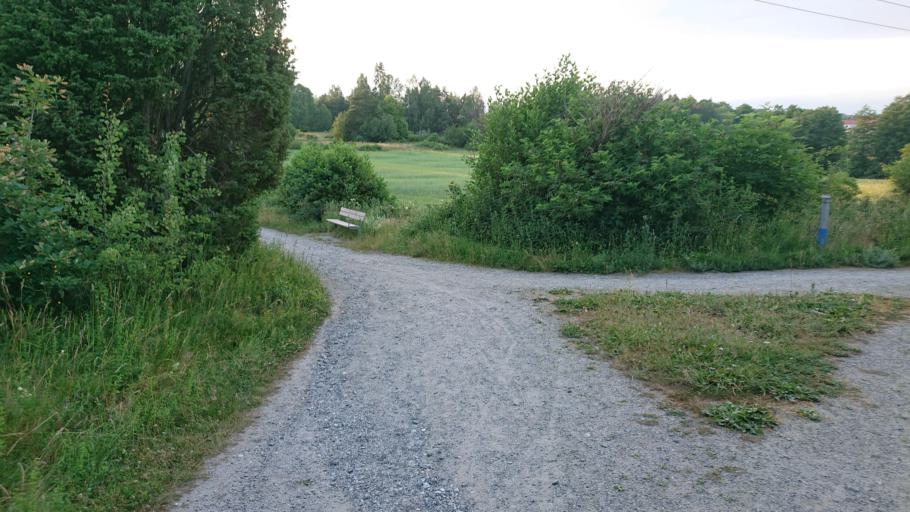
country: SE
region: Stockholm
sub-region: Osterakers Kommun
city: Akersberga
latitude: 59.4961
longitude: 18.2985
